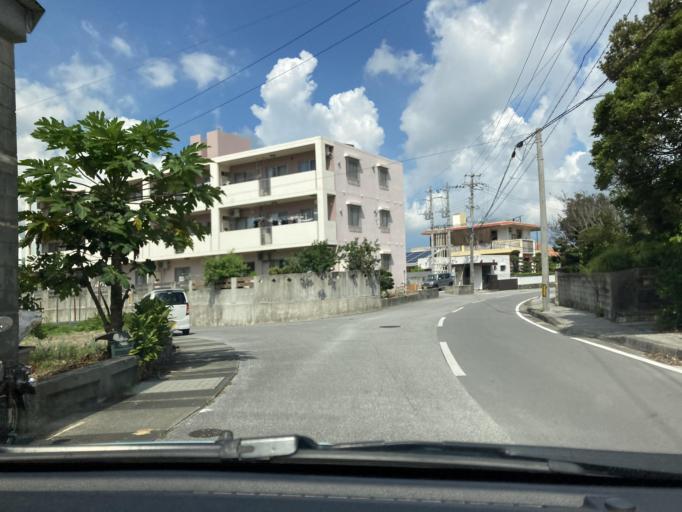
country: JP
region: Okinawa
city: Tomigusuku
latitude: 26.1520
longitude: 127.7547
